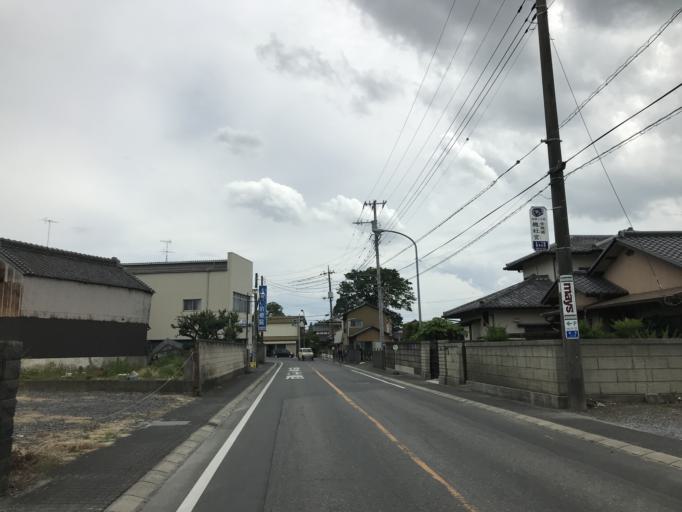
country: JP
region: Ibaraki
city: Ishioka
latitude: 36.1935
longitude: 140.2688
